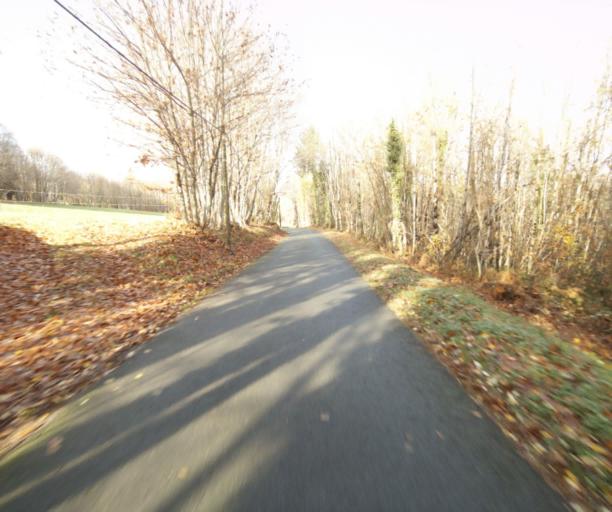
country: FR
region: Limousin
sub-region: Departement de la Correze
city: Sainte-Fortunade
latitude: 45.2168
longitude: 1.7517
